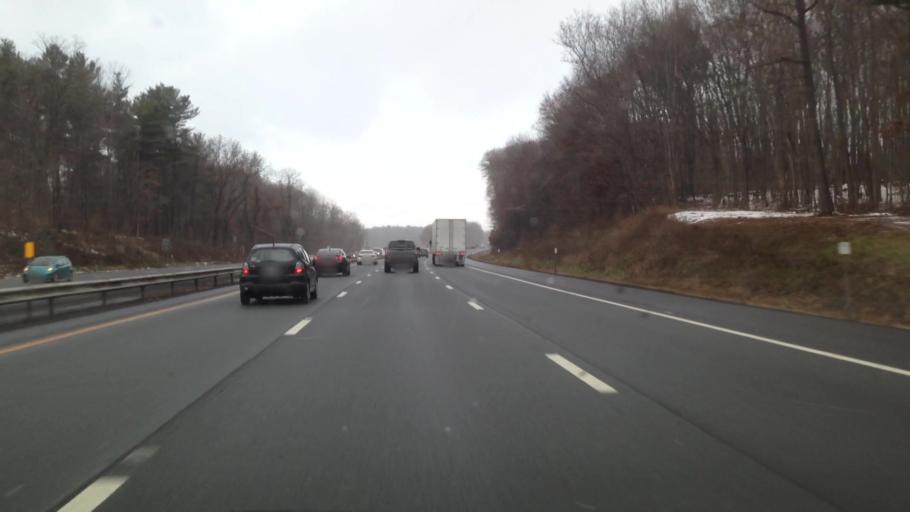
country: US
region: New York
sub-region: Albany County
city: Westmere
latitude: 42.7382
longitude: -73.9076
